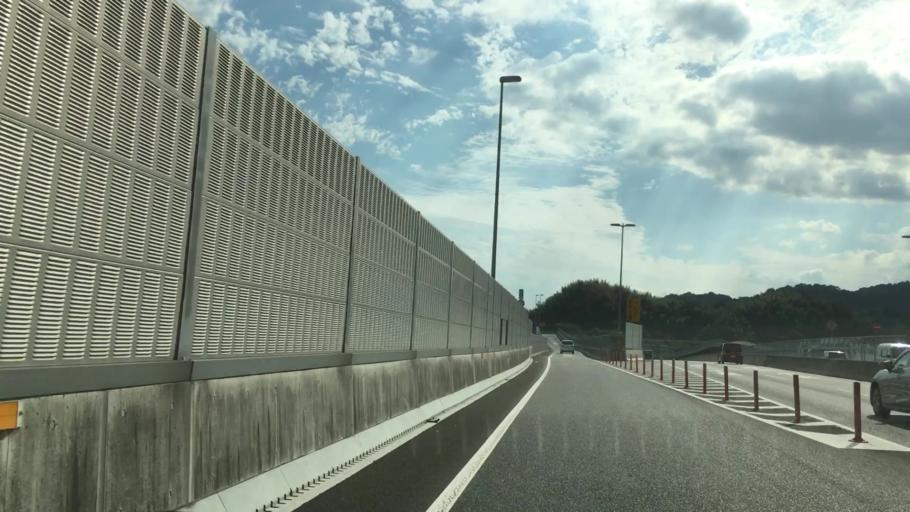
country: JP
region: Hiroshima
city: Hatsukaichi
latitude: 34.3494
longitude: 132.3191
